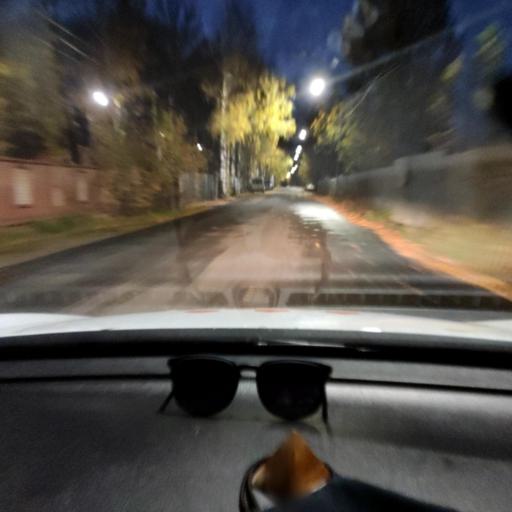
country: RU
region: Tatarstan
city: Verkhniy Uslon
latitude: 55.6008
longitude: 49.0217
